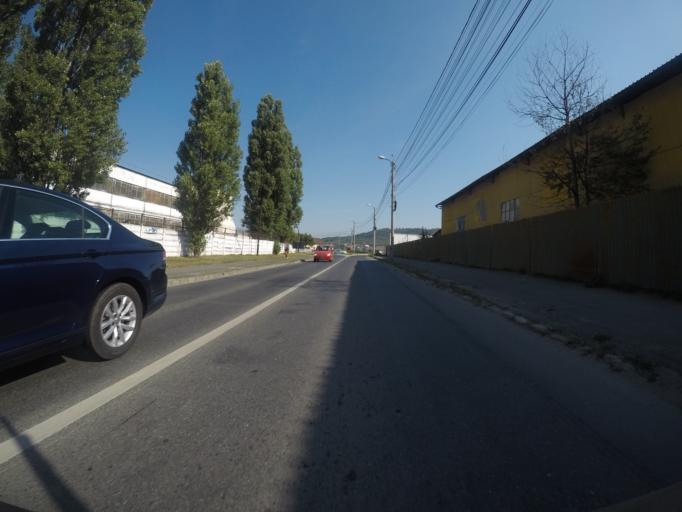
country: RO
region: Sibiu
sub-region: Comuna Selimbar
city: Selimbar
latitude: 45.7939
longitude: 24.1853
